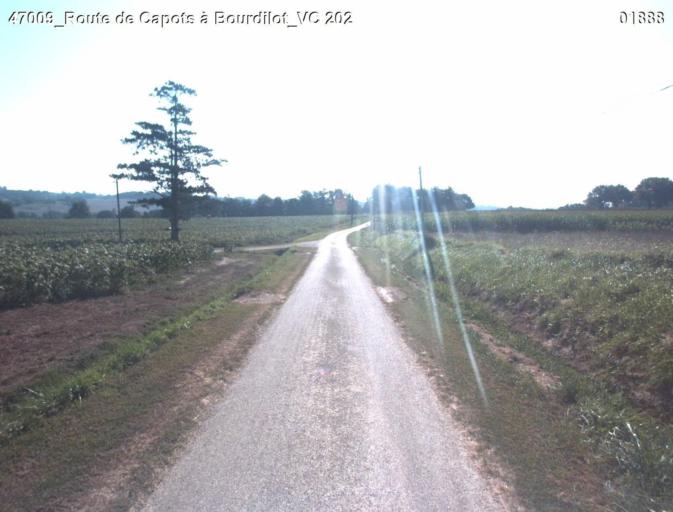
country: FR
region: Aquitaine
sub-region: Departement du Lot-et-Garonne
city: Mezin
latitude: 44.1070
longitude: 0.2921
